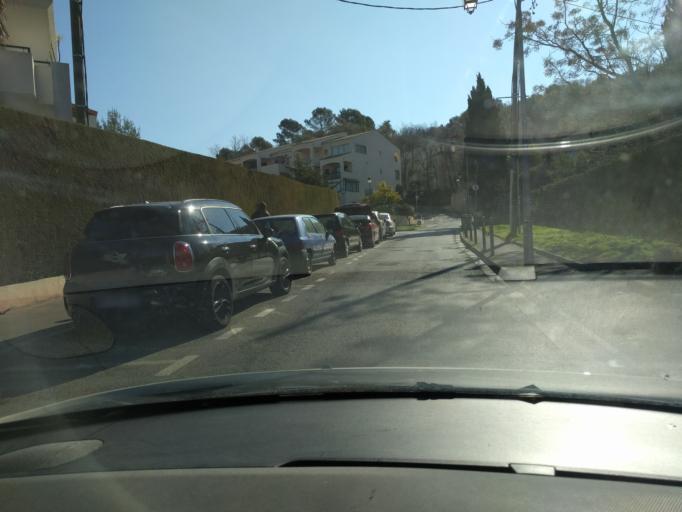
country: FR
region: Provence-Alpes-Cote d'Azur
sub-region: Departement des Alpes-Maritimes
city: Mougins
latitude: 43.6032
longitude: 6.9902
